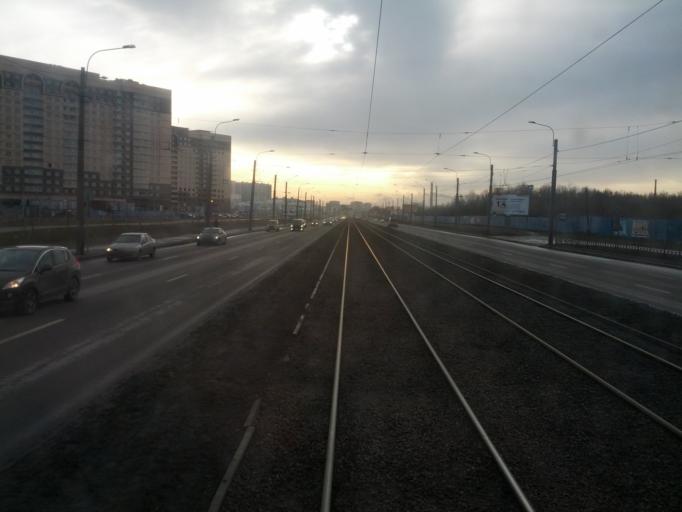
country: RU
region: St.-Petersburg
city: Centralniy
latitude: 59.9168
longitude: 30.4290
